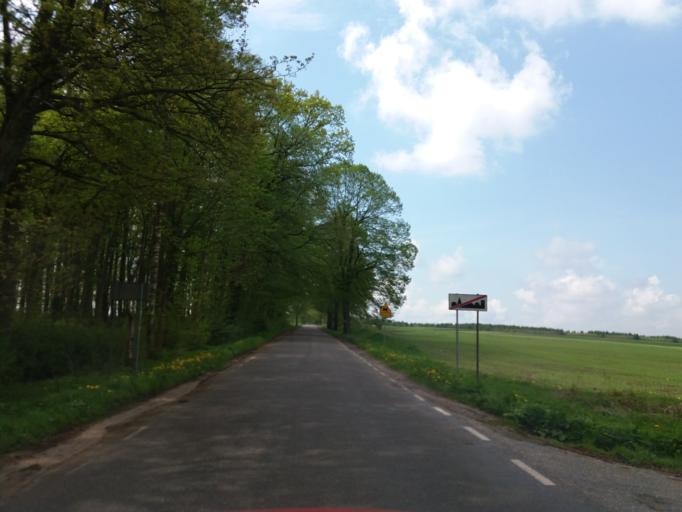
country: PL
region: West Pomeranian Voivodeship
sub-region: Powiat drawski
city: Kalisz Pomorski
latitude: 53.2581
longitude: 15.8510
